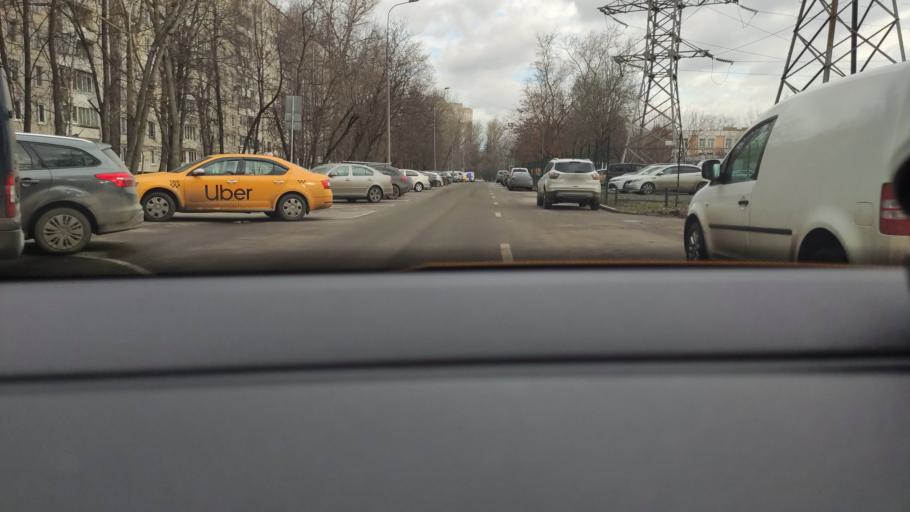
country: RU
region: Moscow
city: Altuf'yevskiy
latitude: 55.8778
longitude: 37.5760
